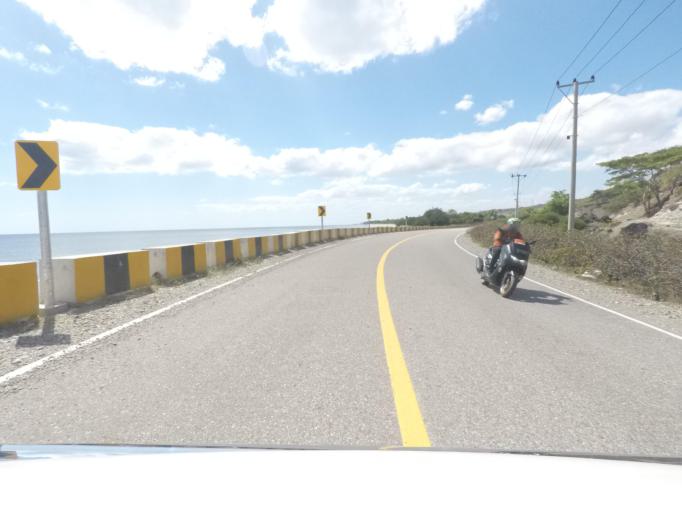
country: TL
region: Baucau
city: Baucau
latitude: -8.4379
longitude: 126.6603
